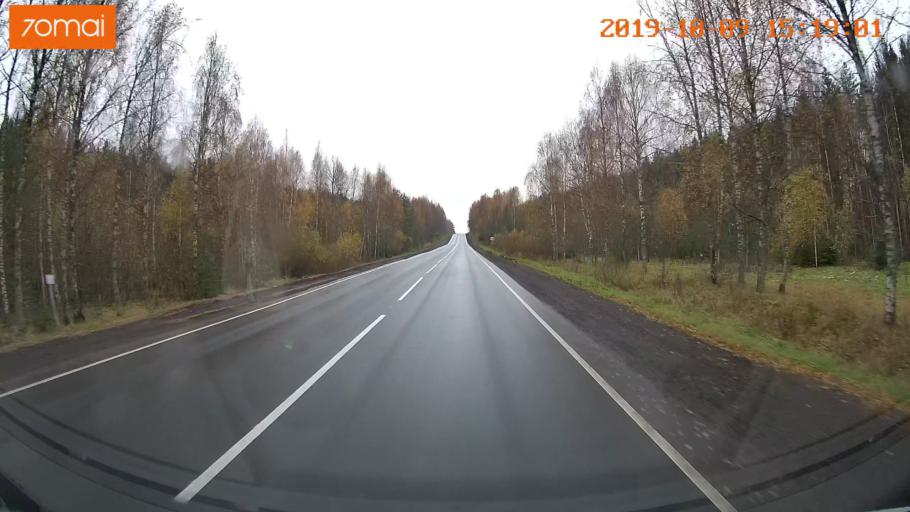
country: RU
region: Kostroma
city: Susanino
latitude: 58.0802
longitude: 41.5639
